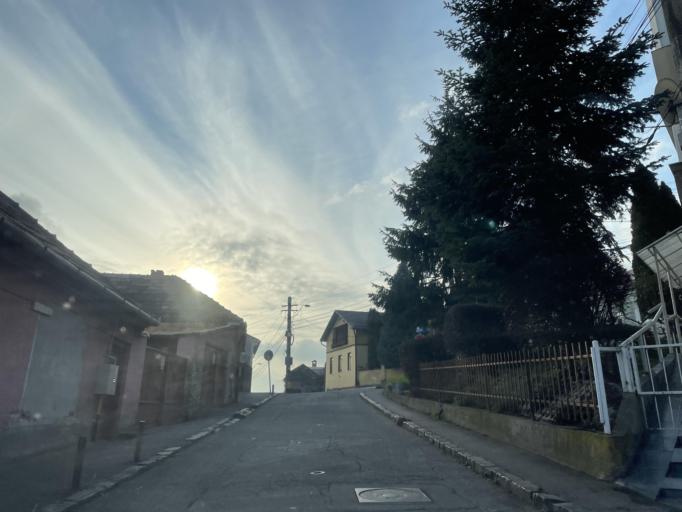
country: RO
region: Mures
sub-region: Municipiul Reghin
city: Reghin
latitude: 46.7777
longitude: 24.7038
